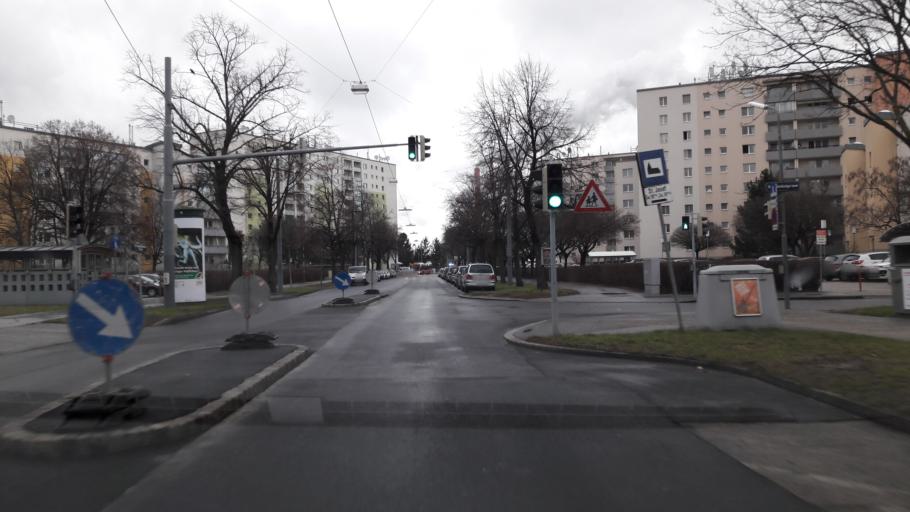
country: AT
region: Lower Austria
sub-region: Politischer Bezirk Wien-Umgebung
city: Schwechat
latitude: 48.1680
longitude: 16.4319
